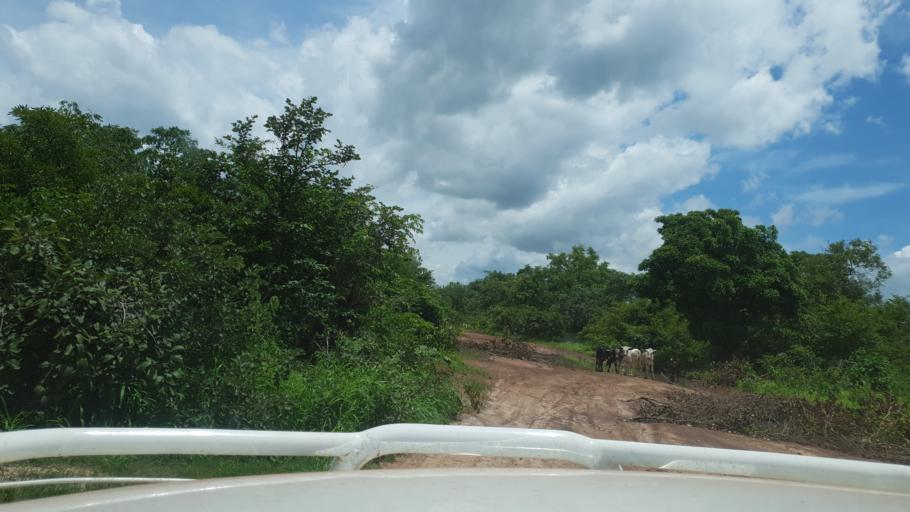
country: ML
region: Koulikoro
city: Banamba
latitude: 13.1998
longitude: -7.3313
